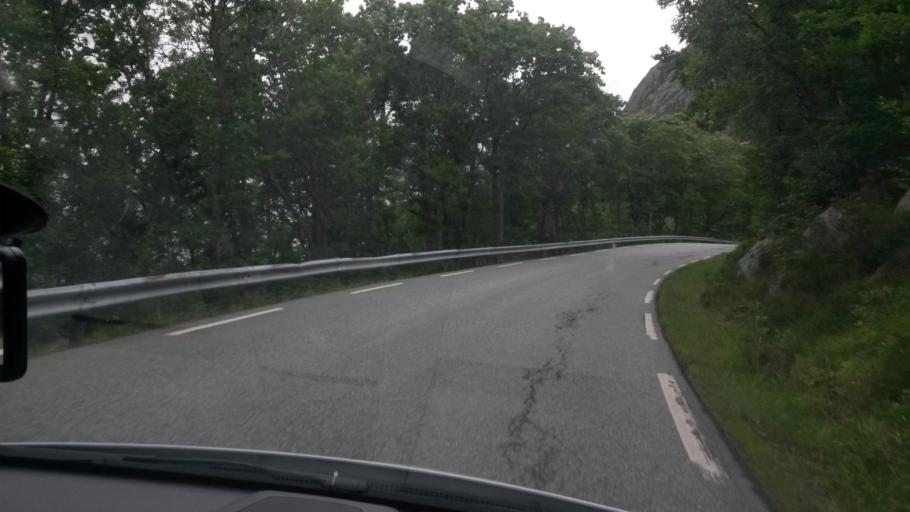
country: NO
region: Rogaland
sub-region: Sandnes
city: Sandnes
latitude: 58.8850
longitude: 5.7756
